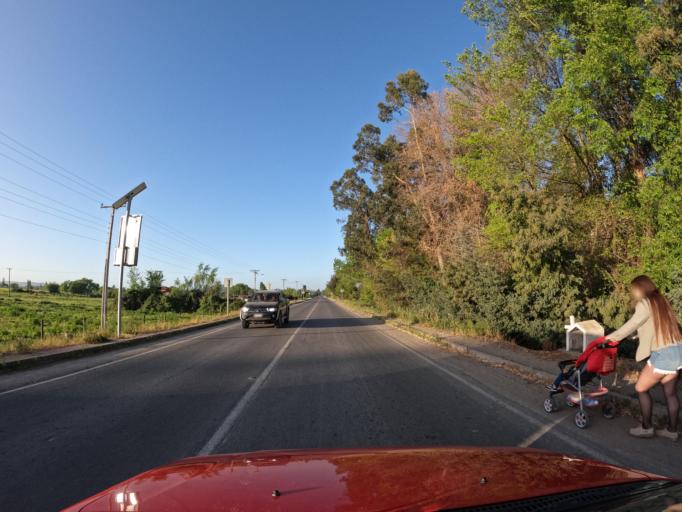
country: CL
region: O'Higgins
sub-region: Provincia de Colchagua
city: Santa Cruz
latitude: -34.3559
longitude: -71.4112
